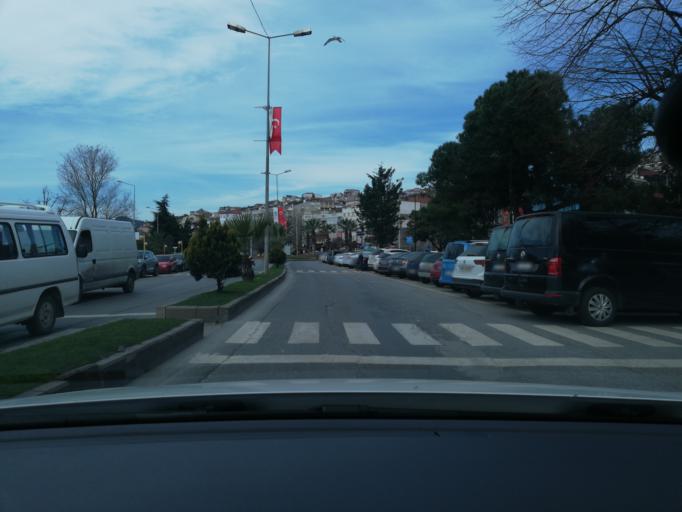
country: TR
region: Zonguldak
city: Eregli
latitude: 41.2787
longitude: 31.4209
